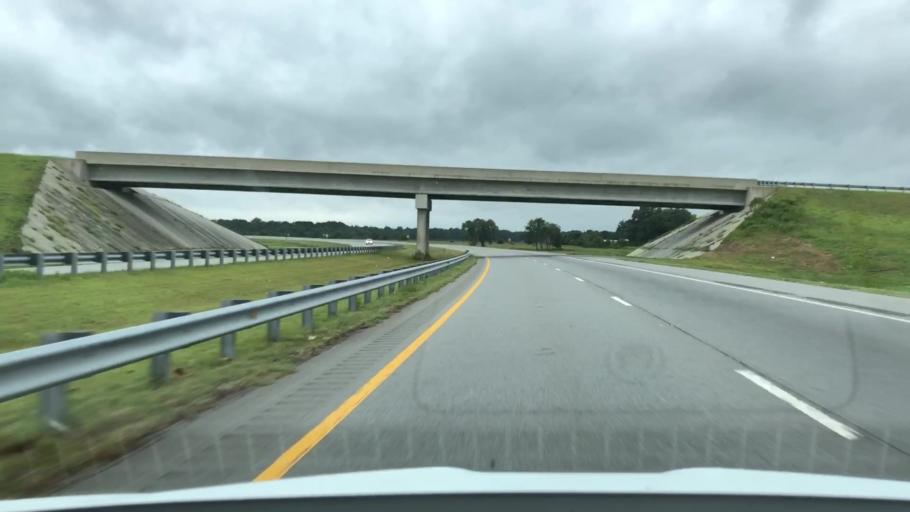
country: US
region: North Carolina
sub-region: Lenoir County
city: Kinston
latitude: 35.2656
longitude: -77.6752
